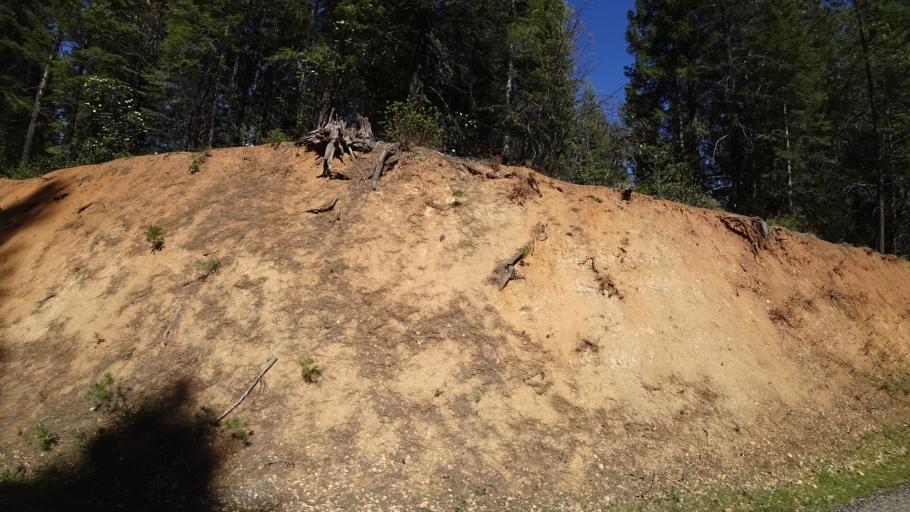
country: US
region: California
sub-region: Trinity County
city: Lewiston
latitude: 40.9030
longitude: -122.7881
